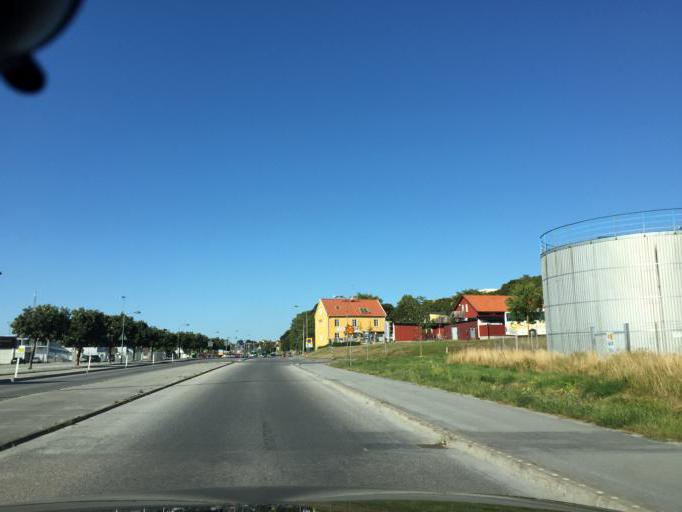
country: SE
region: Gotland
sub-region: Gotland
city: Visby
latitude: 57.6314
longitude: 18.2780
